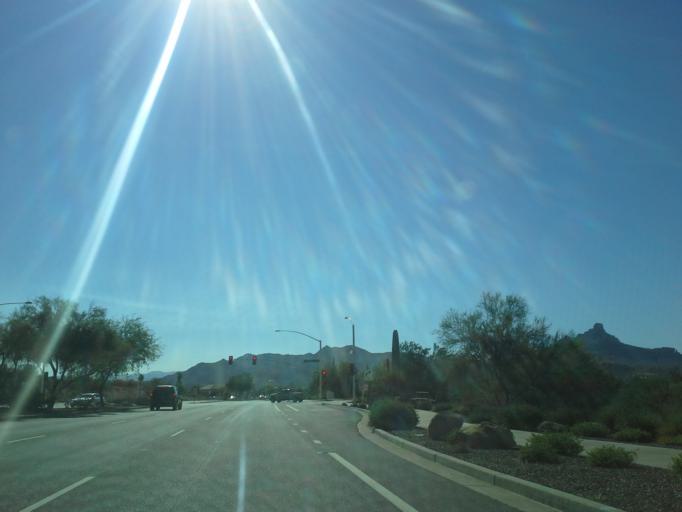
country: US
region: Arizona
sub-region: Maricopa County
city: Fountain Hills
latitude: 33.5755
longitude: -111.7180
